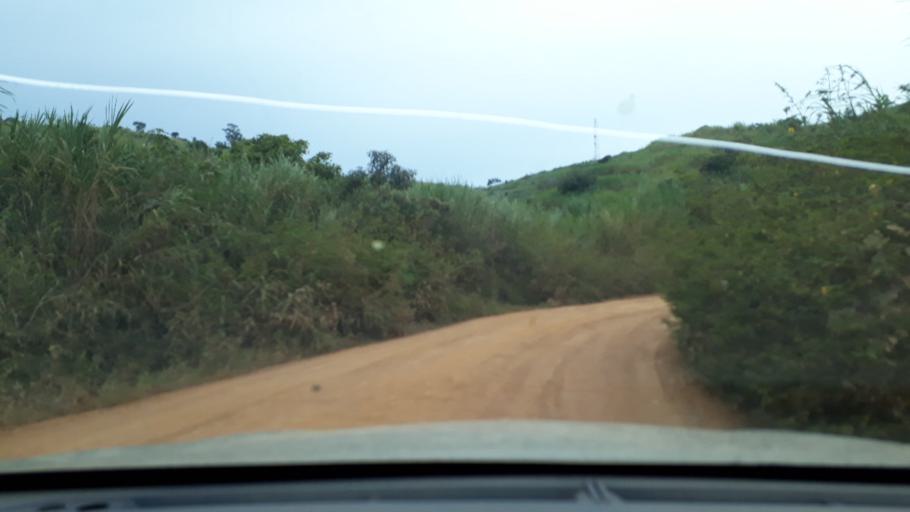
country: CD
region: Eastern Province
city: Bunia
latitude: 1.8199
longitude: 30.4296
